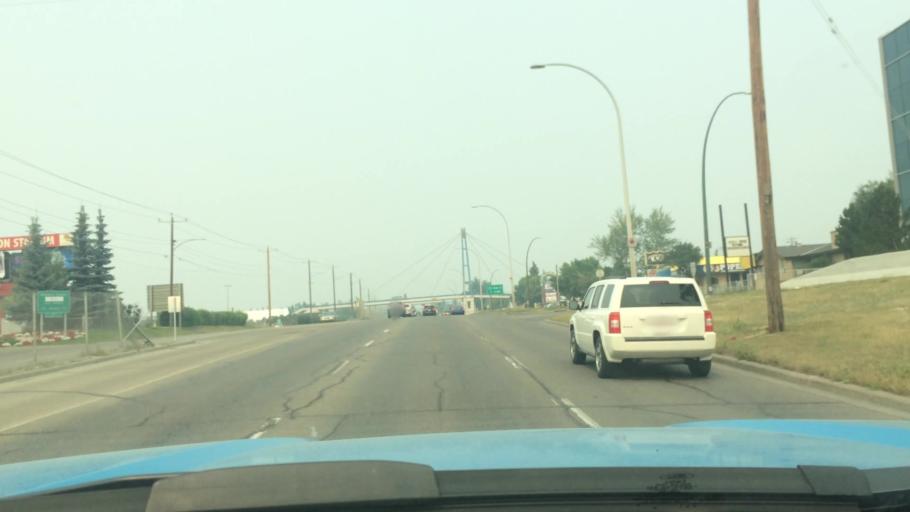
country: CA
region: Alberta
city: Calgary
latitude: 51.0686
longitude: -114.1178
